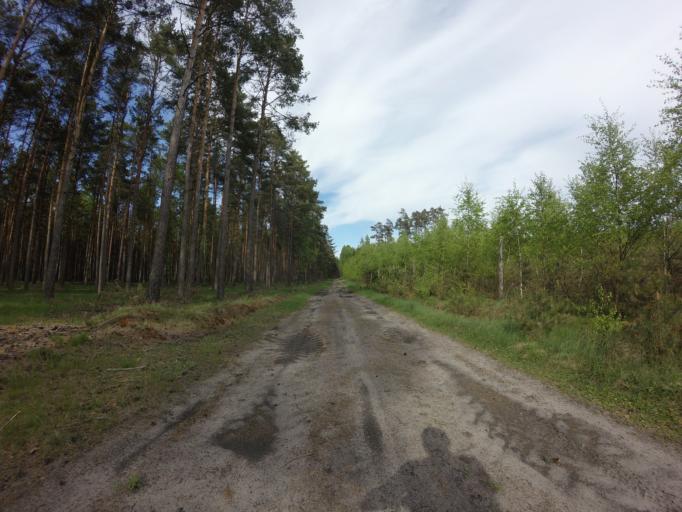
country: PL
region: West Pomeranian Voivodeship
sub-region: Powiat choszczenski
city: Drawno
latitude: 53.1883
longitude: 15.7289
